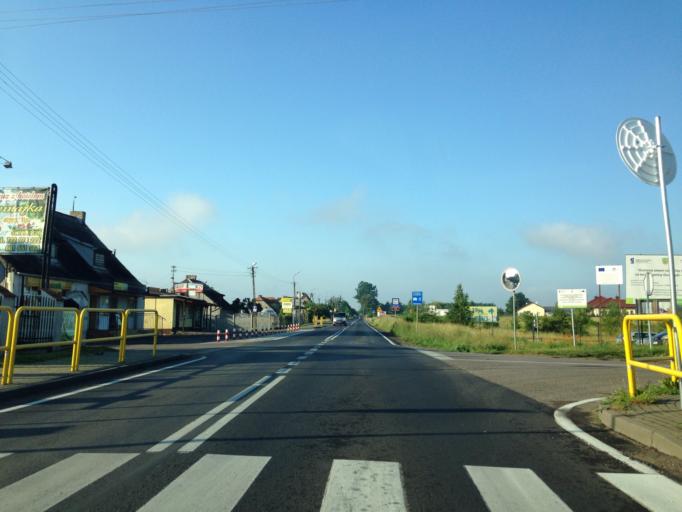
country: PL
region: Kujawsko-Pomorskie
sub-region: Grudziadz
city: Grudziadz
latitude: 53.5233
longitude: 18.8111
